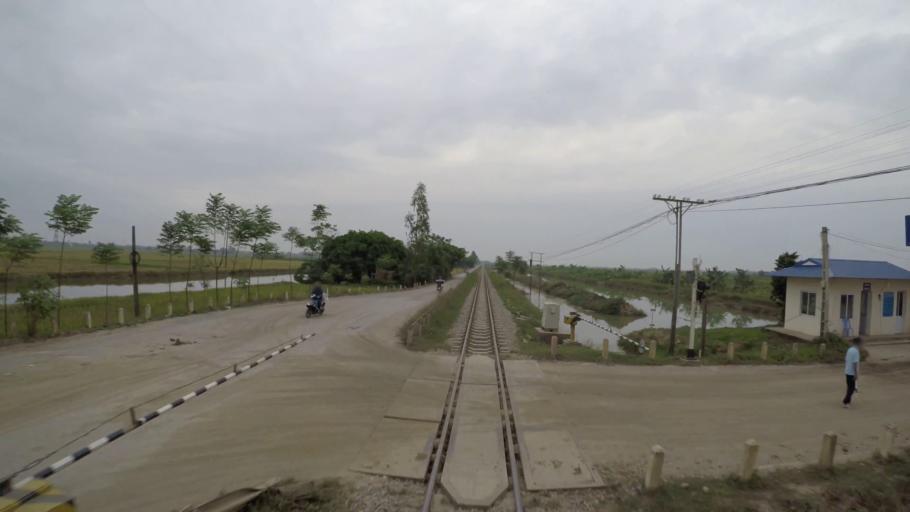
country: VN
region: Hai Duong
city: Ke Sat
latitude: 20.9655
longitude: 106.1194
